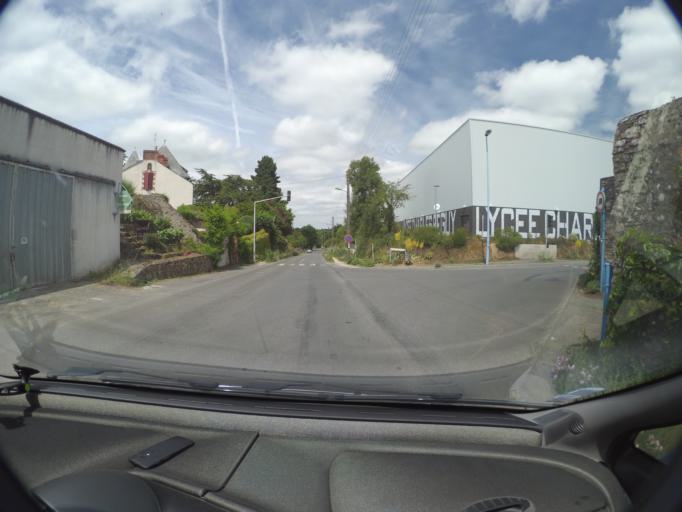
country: FR
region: Pays de la Loire
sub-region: Departement de la Loire-Atlantique
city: Gorges
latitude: 47.1030
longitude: -1.3043
